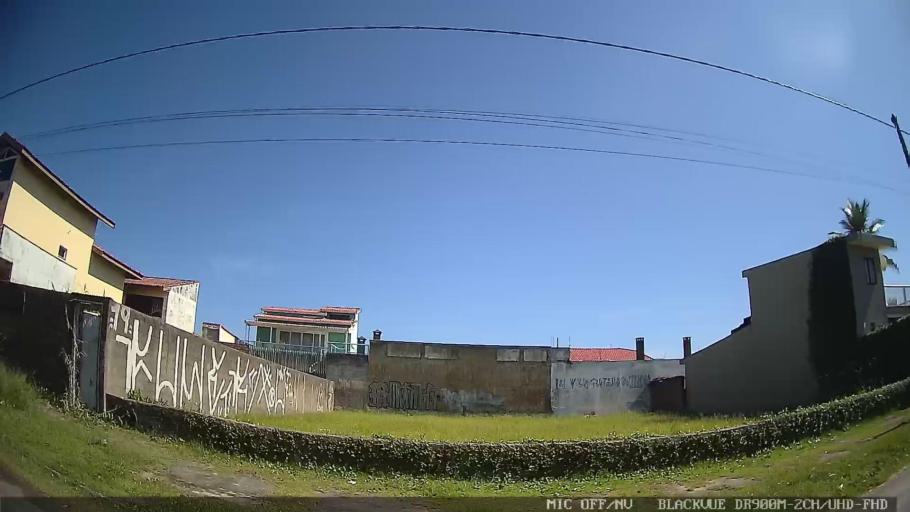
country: BR
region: Sao Paulo
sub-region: Peruibe
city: Peruibe
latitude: -24.2847
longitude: -46.9484
